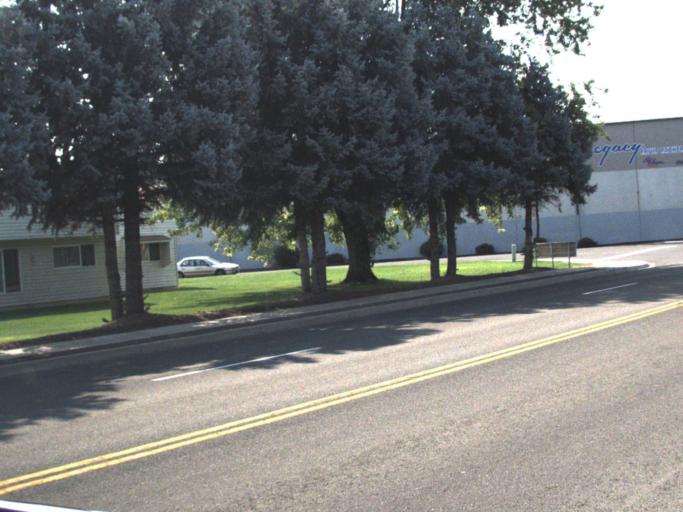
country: US
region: Washington
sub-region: Yakima County
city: Selah
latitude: 46.6573
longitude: -120.5263
